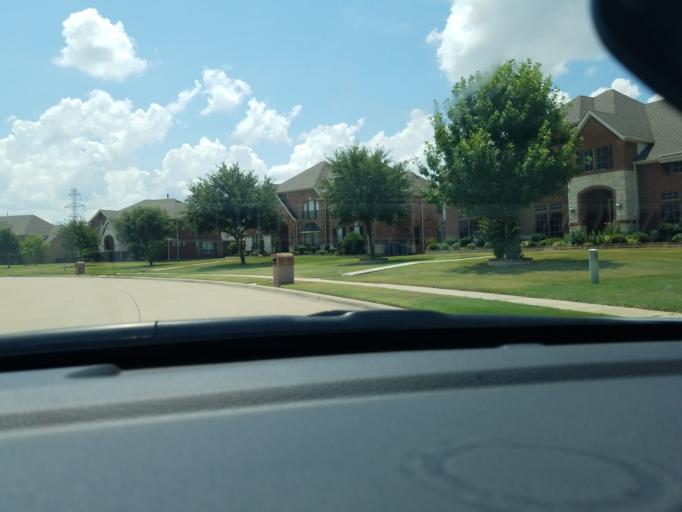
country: US
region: Texas
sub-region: Dallas County
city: Sunnyvale
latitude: 32.8065
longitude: -96.5807
